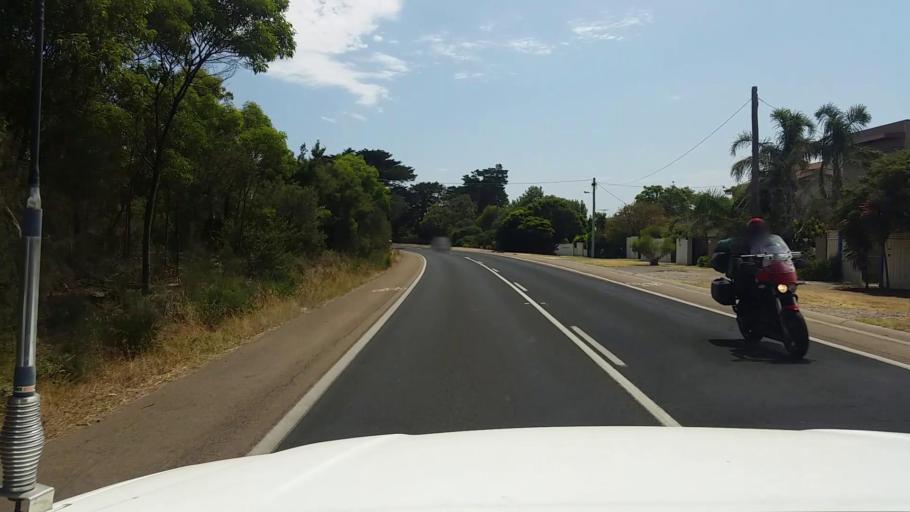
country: AU
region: Victoria
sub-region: Mornington Peninsula
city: Mornington
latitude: -38.2392
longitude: 145.0296
